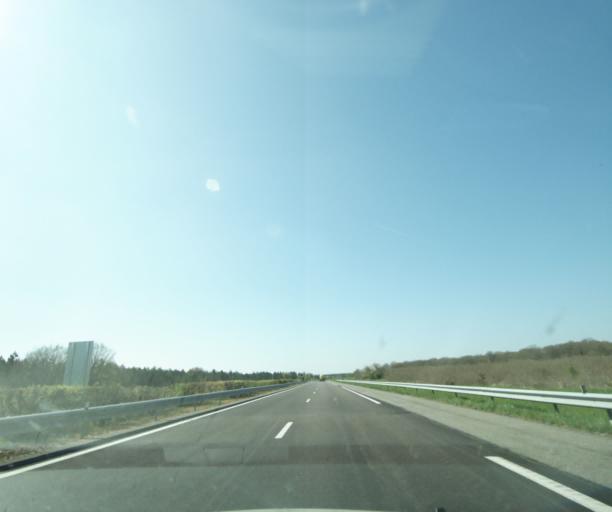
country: FR
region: Centre
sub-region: Departement du Loiret
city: Ouzouer-sur-Trezee
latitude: 47.6188
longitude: 2.8066
